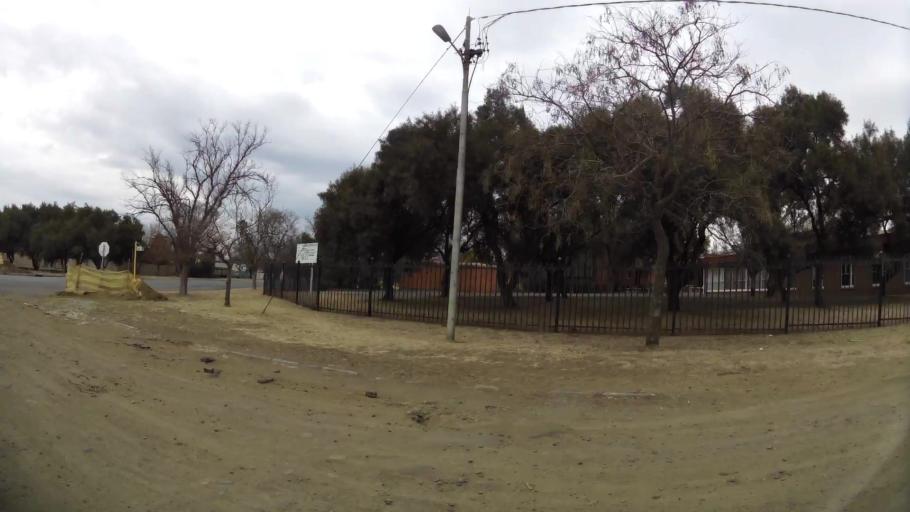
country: ZA
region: Orange Free State
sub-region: Fezile Dabi District Municipality
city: Kroonstad
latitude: -27.6795
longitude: 27.2338
